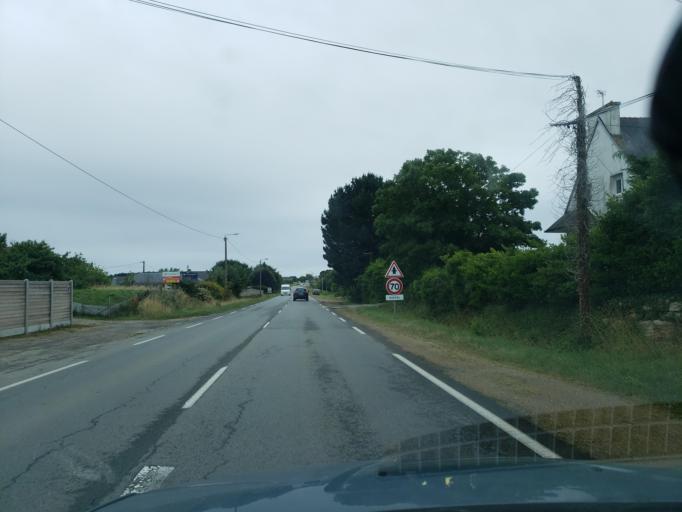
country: FR
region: Brittany
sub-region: Departement du Finistere
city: Guilvinec
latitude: 47.8132
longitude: -4.2838
